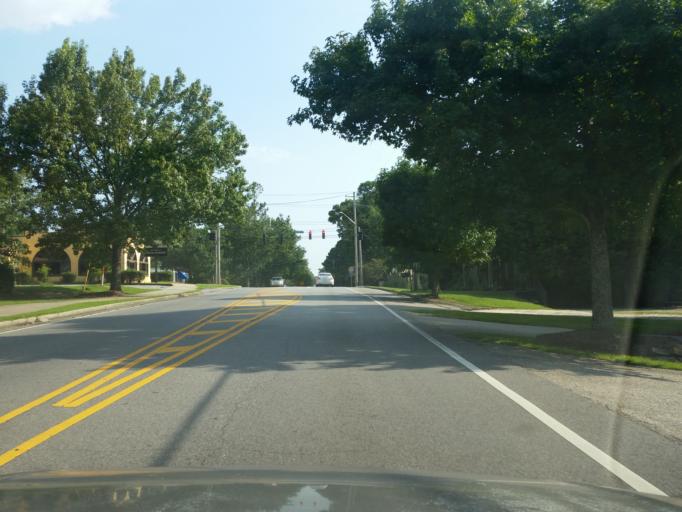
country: US
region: Alabama
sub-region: Baldwin County
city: Fairhope
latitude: 30.5407
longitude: -87.8987
